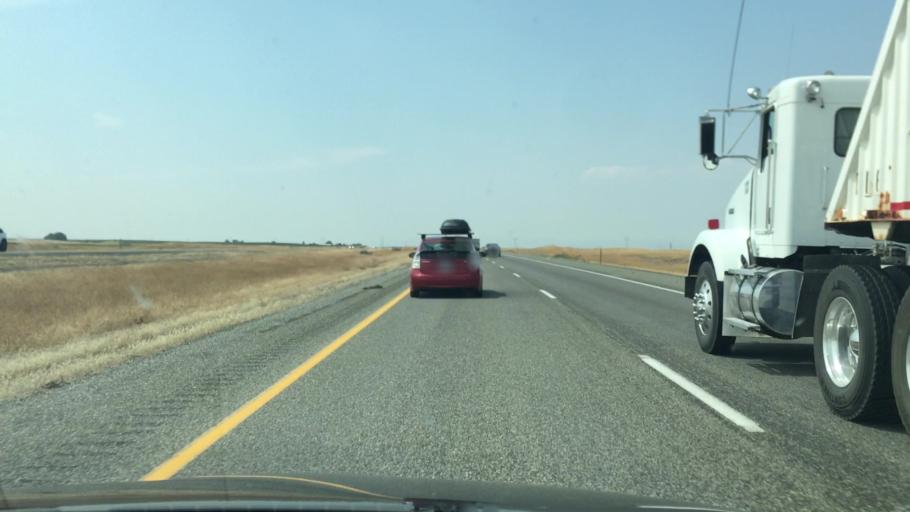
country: US
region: Idaho
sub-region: Gooding County
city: Wendell
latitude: 42.8203
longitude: -114.7883
